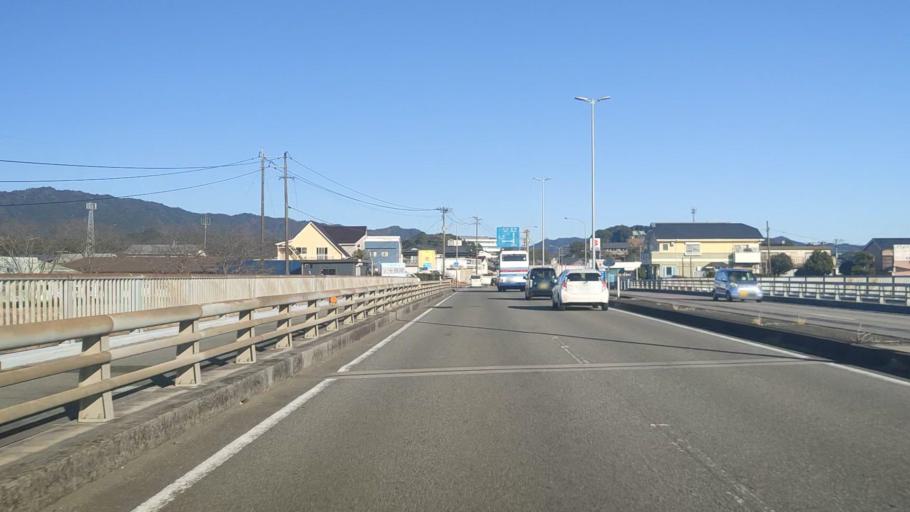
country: JP
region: Miyazaki
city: Nobeoka
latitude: 32.4646
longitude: 131.6484
